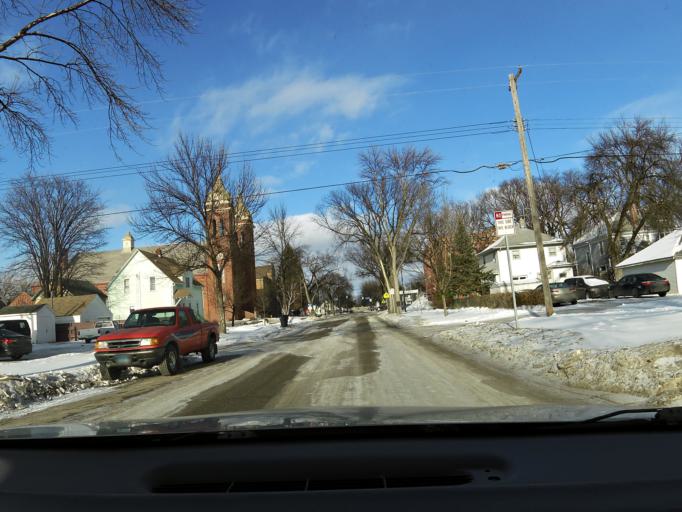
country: US
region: North Dakota
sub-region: Grand Forks County
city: Grand Forks
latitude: 47.9257
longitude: -97.0401
